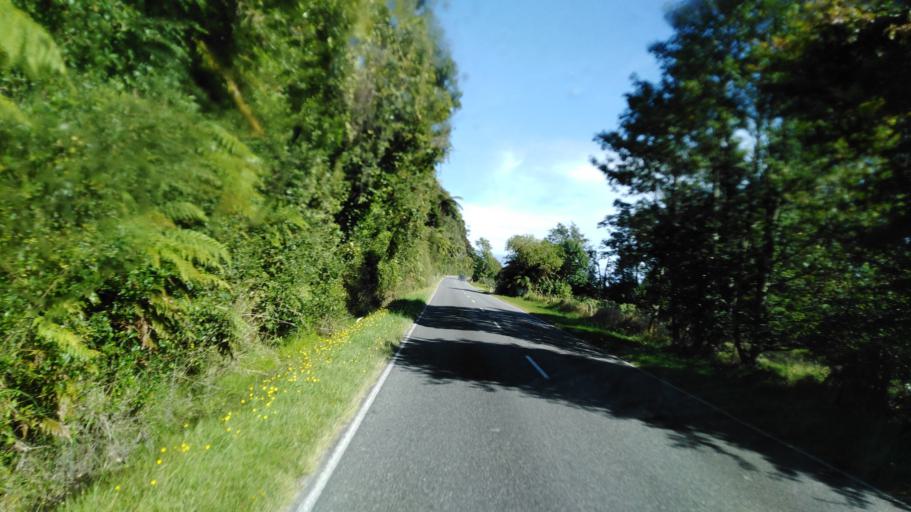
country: NZ
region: West Coast
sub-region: Buller District
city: Westport
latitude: -41.2596
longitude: 172.1206
